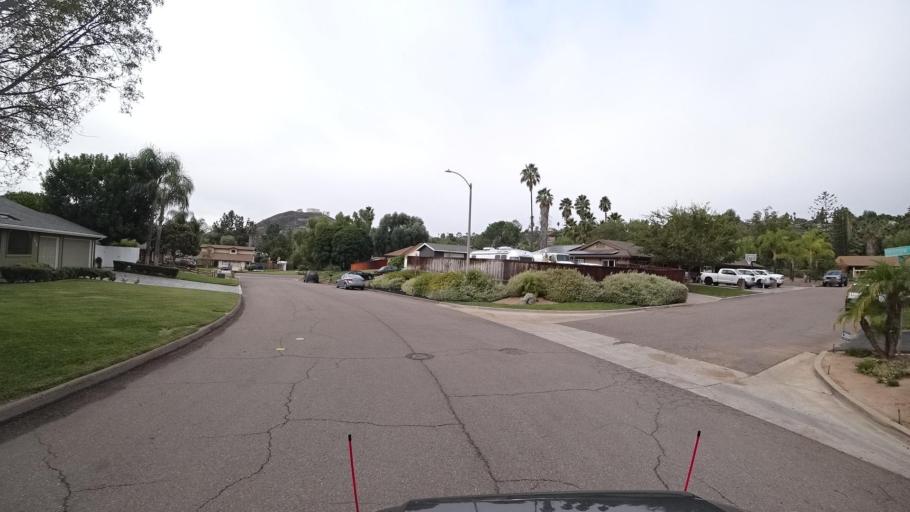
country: US
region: California
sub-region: San Diego County
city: Rancho San Diego
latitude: 32.7649
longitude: -116.9259
